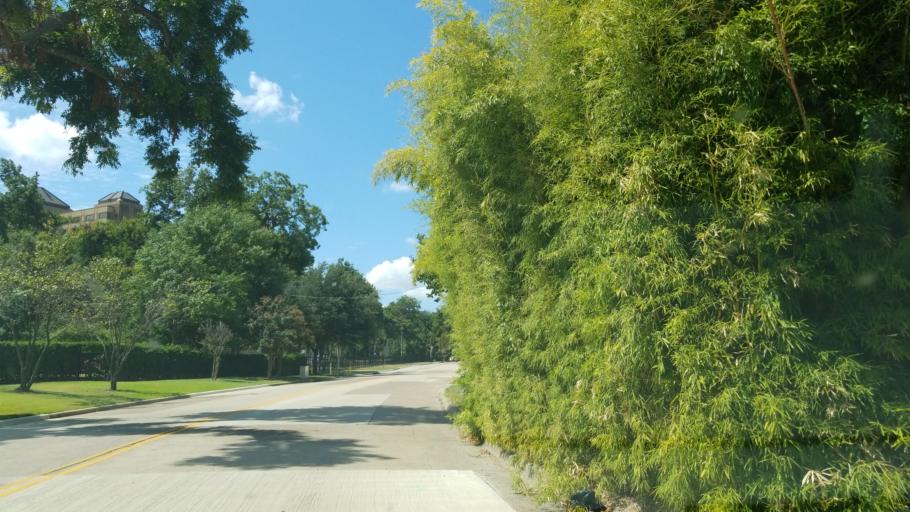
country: US
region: Texas
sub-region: Dallas County
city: Dallas
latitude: 32.7634
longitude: -96.8240
